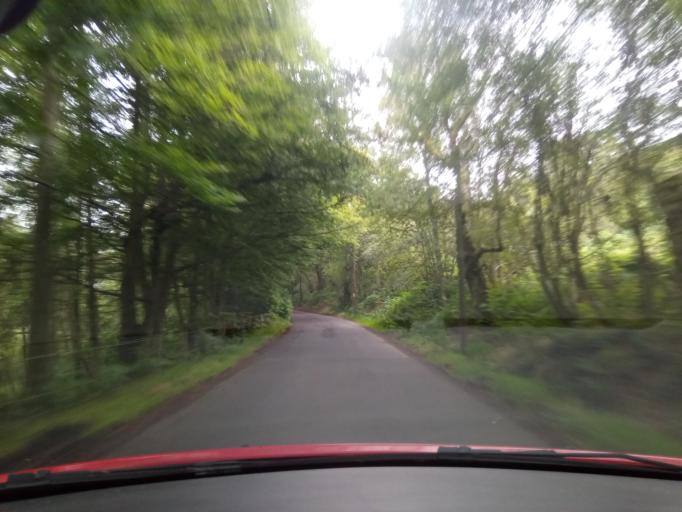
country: GB
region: England
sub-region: Northumberland
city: Otterburn
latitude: 55.2940
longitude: -2.0538
